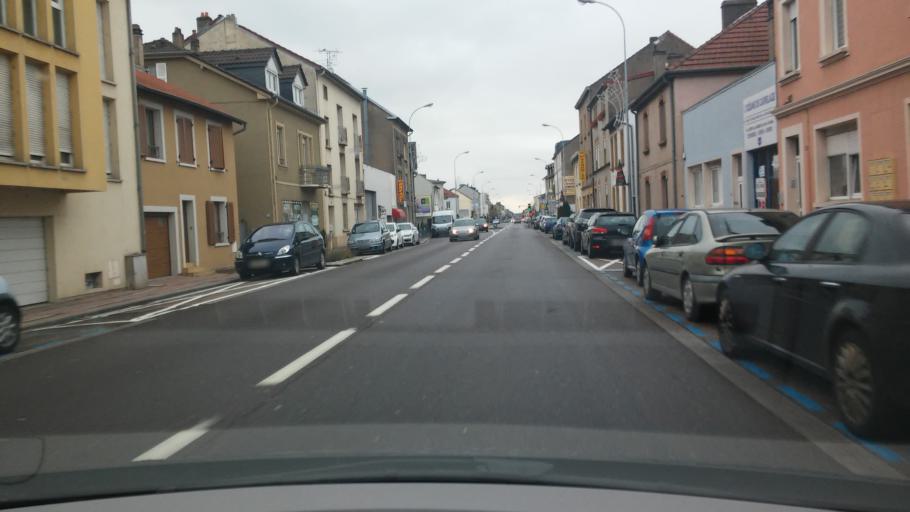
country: FR
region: Lorraine
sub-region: Departement de la Moselle
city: Hagondange
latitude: 49.2515
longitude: 6.1699
